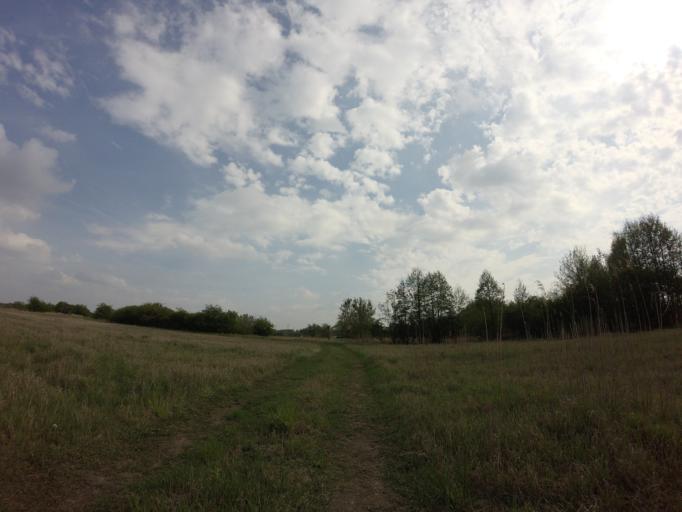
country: PL
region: West Pomeranian Voivodeship
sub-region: Powiat choszczenski
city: Choszczno
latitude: 53.1734
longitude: 15.3894
